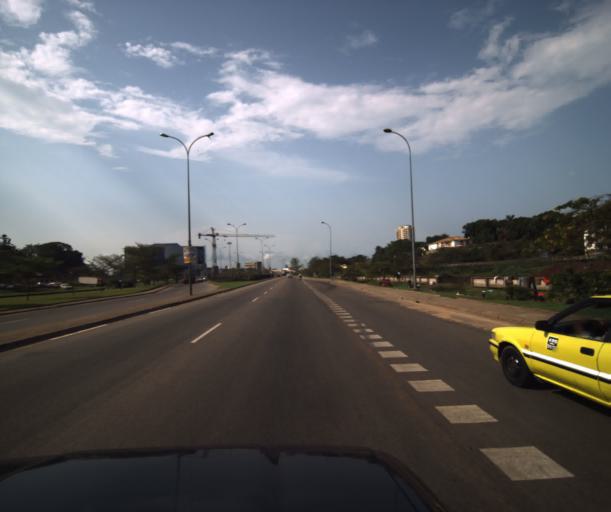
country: CM
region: Littoral
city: Douala
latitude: 4.0446
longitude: 9.6906
